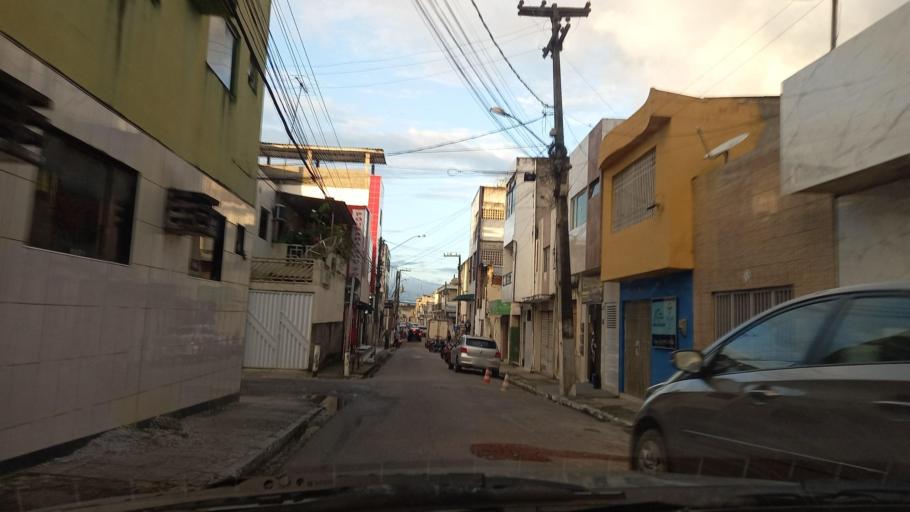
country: BR
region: Pernambuco
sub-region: Palmares
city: Palmares
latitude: -8.6848
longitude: -35.5912
